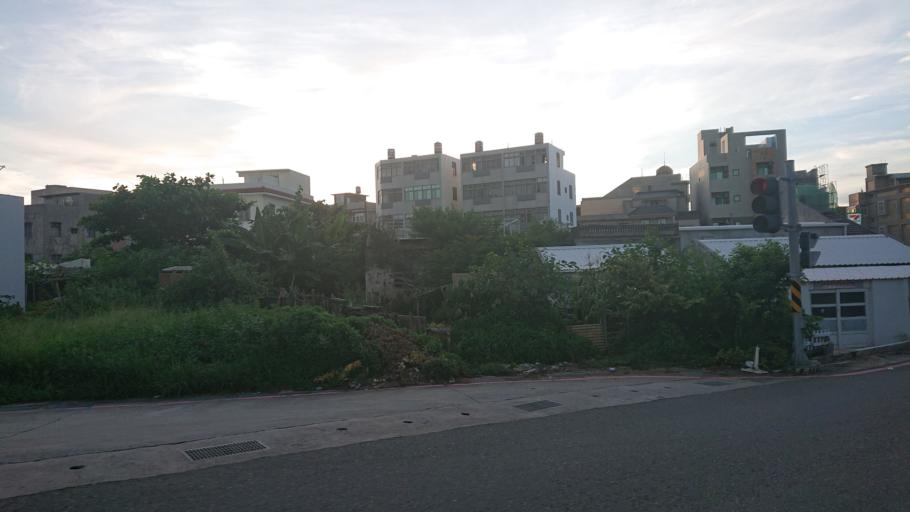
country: TW
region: Taiwan
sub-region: Penghu
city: Ma-kung
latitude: 23.5791
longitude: 119.5799
